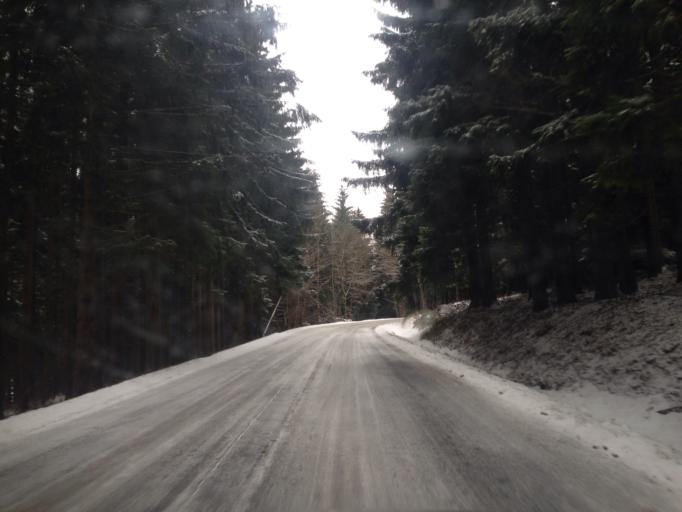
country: CZ
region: Liberecky
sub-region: Okres Semily
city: Vysoke nad Jizerou
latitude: 50.7152
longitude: 15.3723
